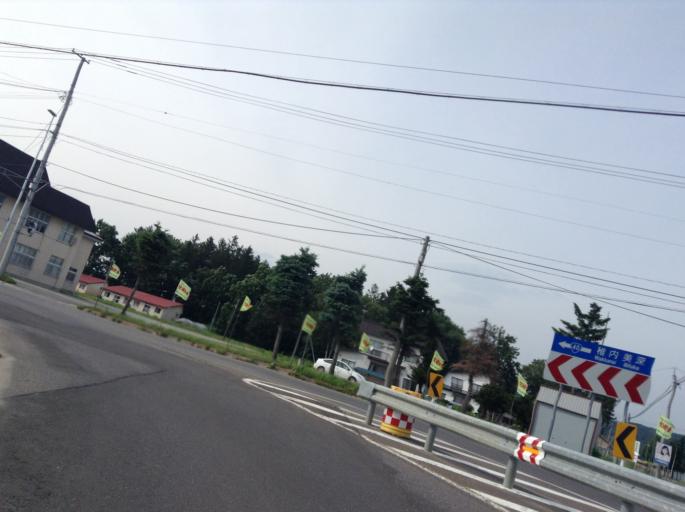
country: JP
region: Hokkaido
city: Nayoro
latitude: 44.4368
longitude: 142.4033
